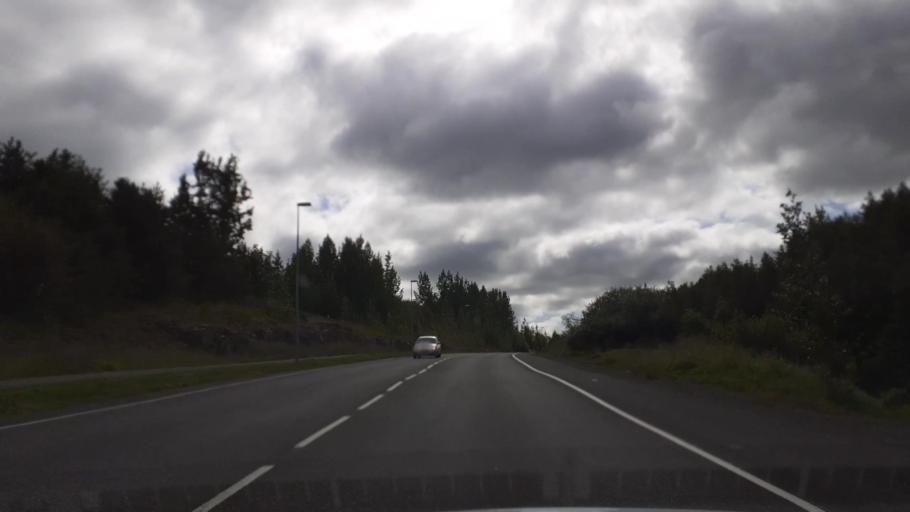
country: IS
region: Northeast
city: Akureyri
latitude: 65.6833
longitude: -18.1156
